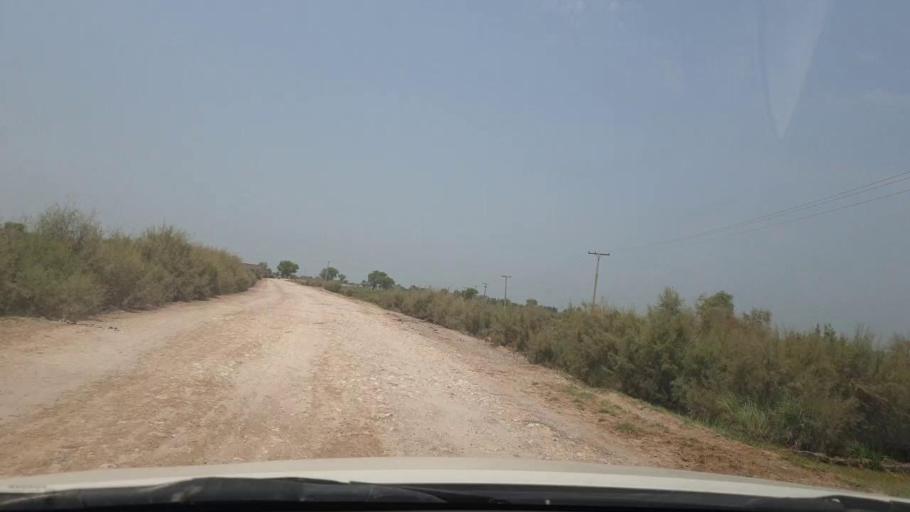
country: PK
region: Sindh
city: Rustam jo Goth
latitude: 28.0349
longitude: 68.7566
